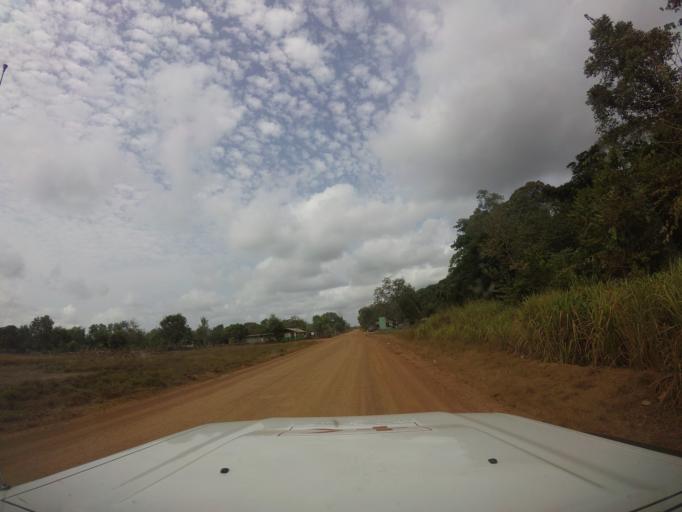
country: LR
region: Grand Cape Mount
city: Robertsport
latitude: 6.6955
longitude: -11.1036
